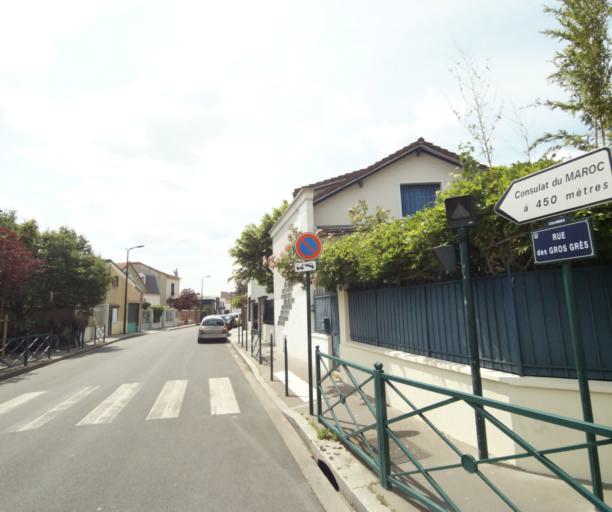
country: FR
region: Ile-de-France
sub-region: Departement des Hauts-de-Seine
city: Colombes
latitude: 48.9166
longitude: 2.2427
